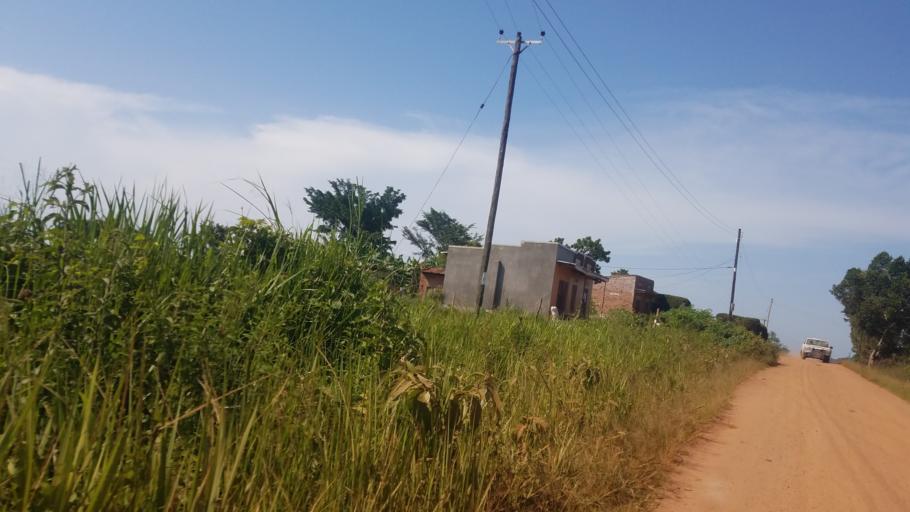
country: UG
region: Central Region
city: Masaka
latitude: -0.3055
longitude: 31.6834
